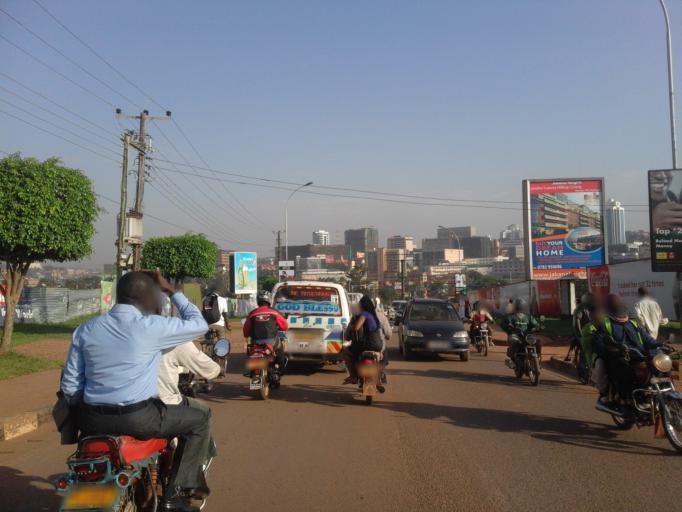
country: UG
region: Central Region
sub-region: Kampala District
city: Kampala
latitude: 0.3057
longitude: 32.5837
